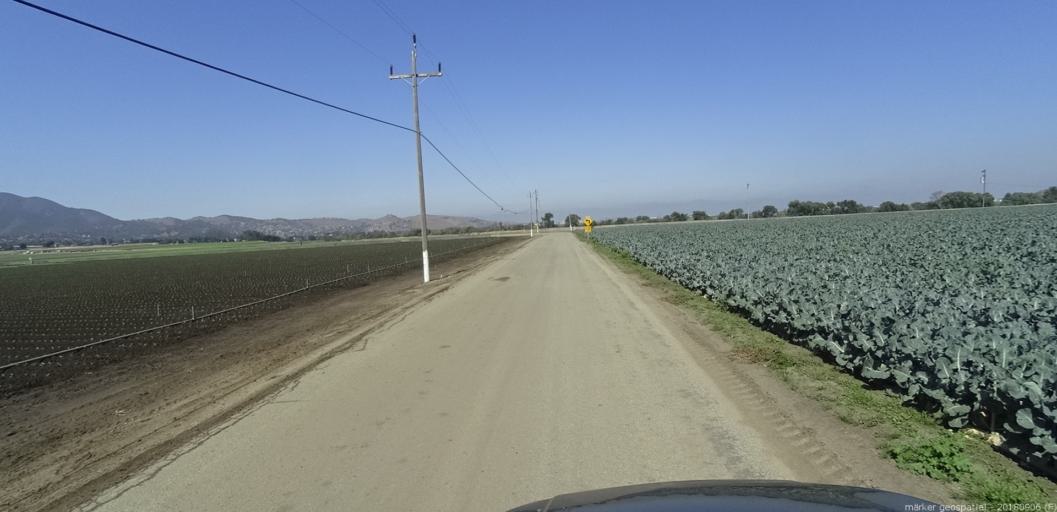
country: US
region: California
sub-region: Monterey County
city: Salinas
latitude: 36.6011
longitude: -121.6137
